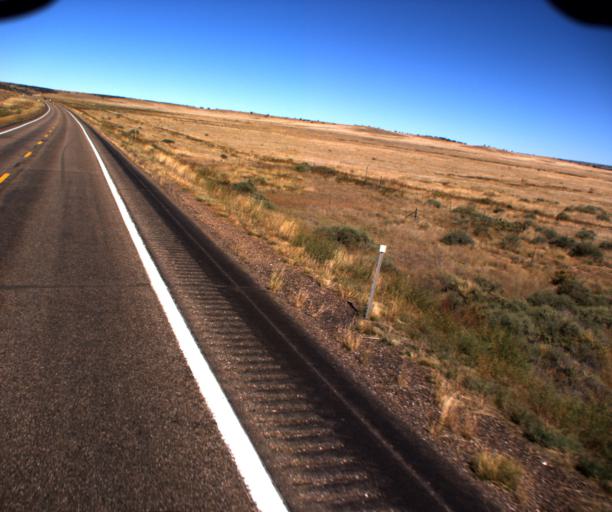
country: US
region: Arizona
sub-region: Apache County
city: Saint Johns
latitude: 34.3164
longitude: -109.3815
